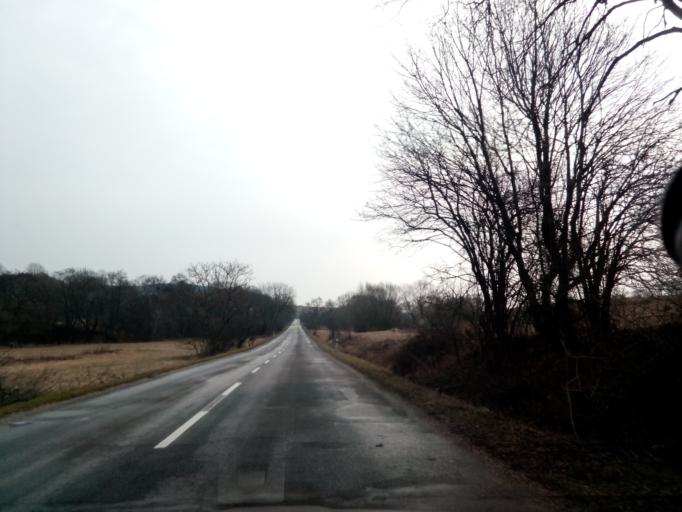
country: SK
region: Kosicky
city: Secovce
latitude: 48.6327
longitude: 21.5135
